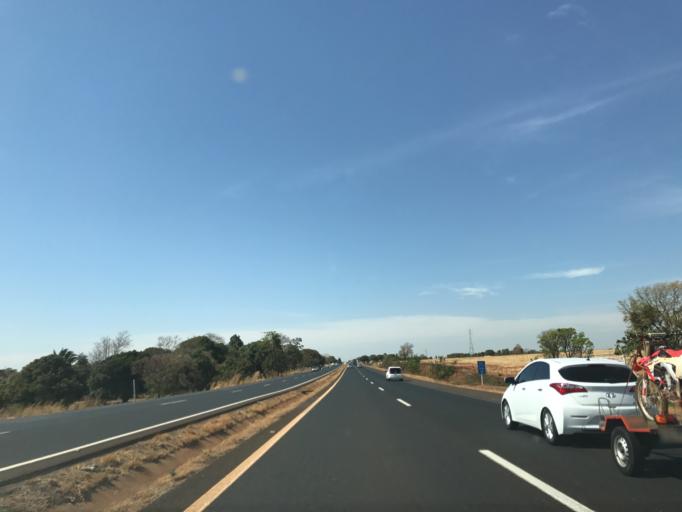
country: BR
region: Minas Gerais
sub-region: Centralina
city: Centralina
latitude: -18.6925
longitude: -49.1488
